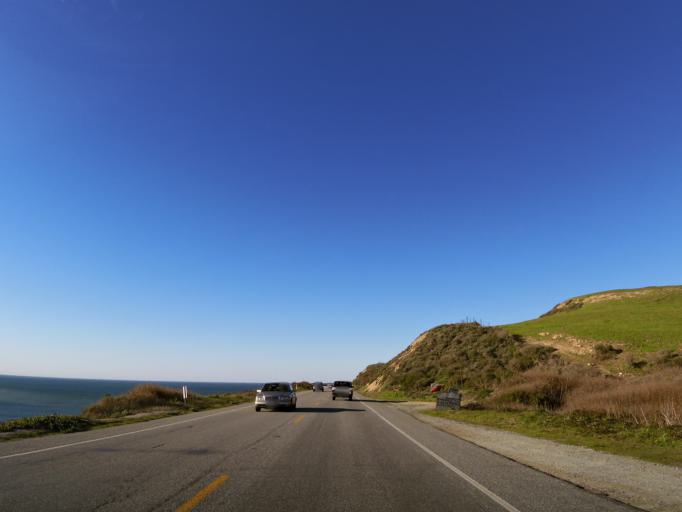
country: US
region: California
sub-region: Santa Cruz County
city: Bonny Doon
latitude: 37.0504
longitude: -122.2401
